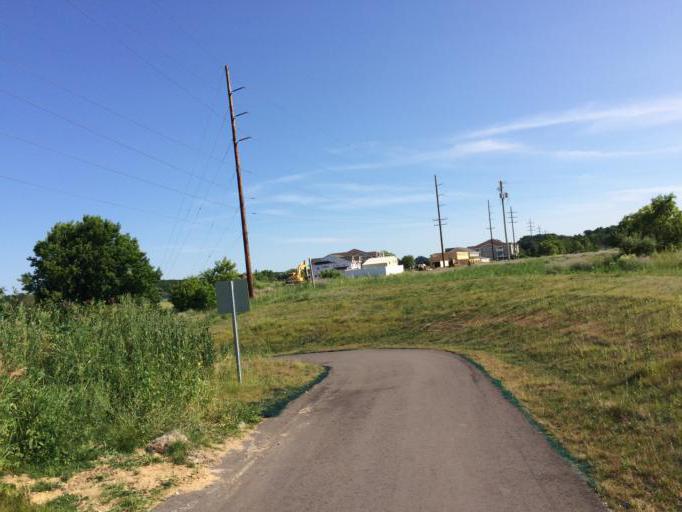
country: US
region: Michigan
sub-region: Grand Traverse County
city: Traverse City
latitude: 44.7552
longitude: -85.6167
